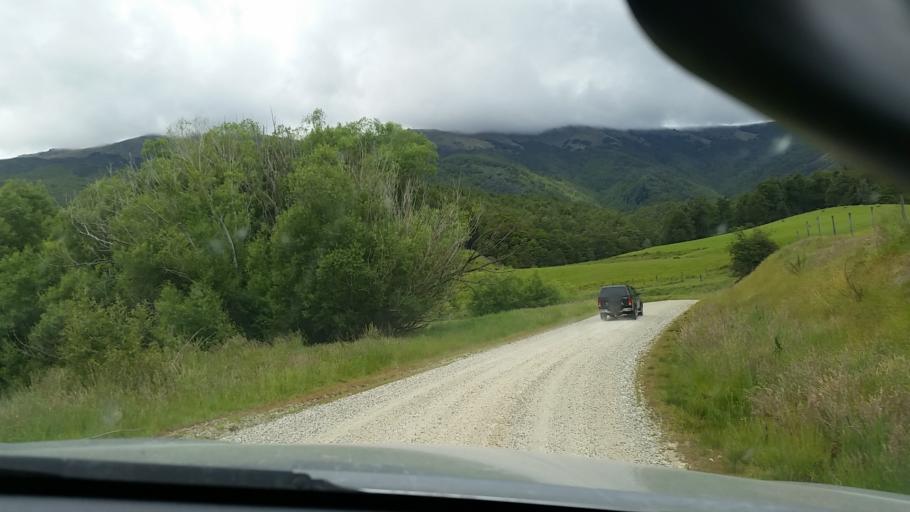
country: NZ
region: Otago
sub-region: Queenstown-Lakes District
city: Kingston
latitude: -45.5826
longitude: 168.9998
